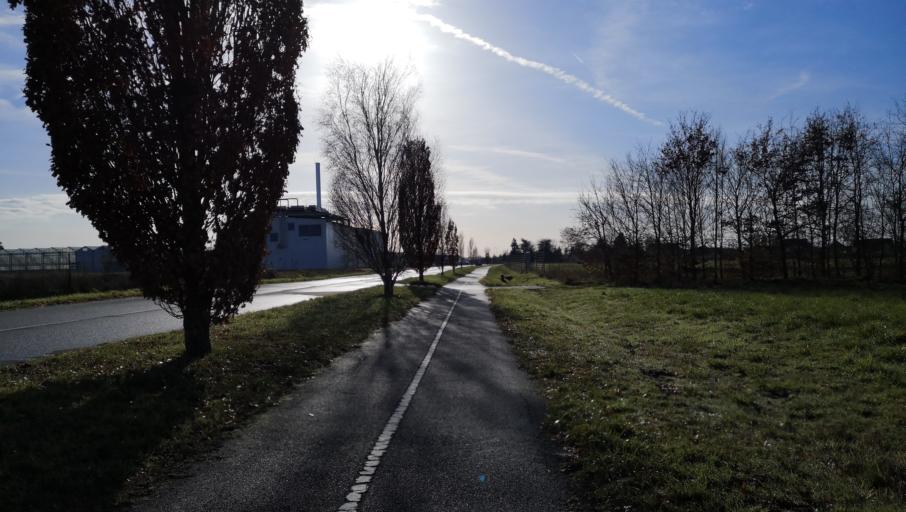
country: FR
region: Centre
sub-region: Departement du Loiret
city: Saint-Denis-en-Val
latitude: 47.8758
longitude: 1.9794
